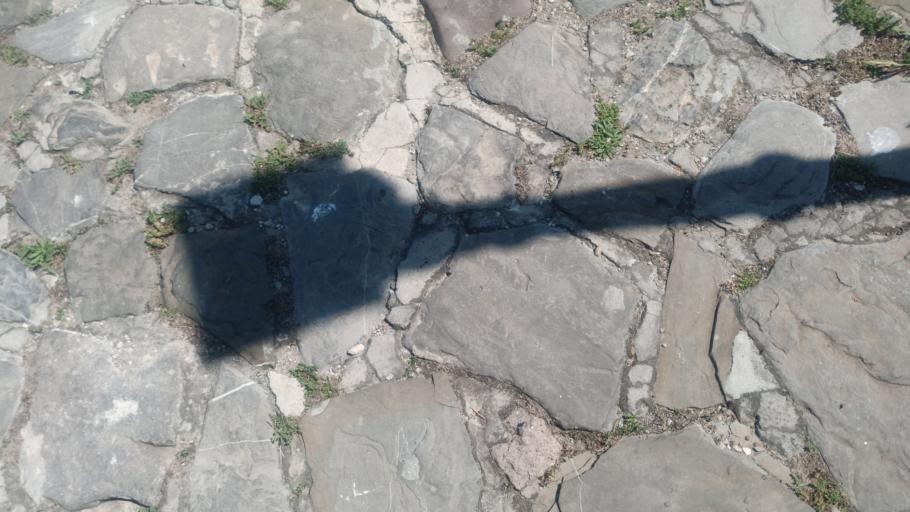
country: BG
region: Burgas
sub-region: Obshtina Nesebur
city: Nesebar
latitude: 42.6594
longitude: 27.7343
